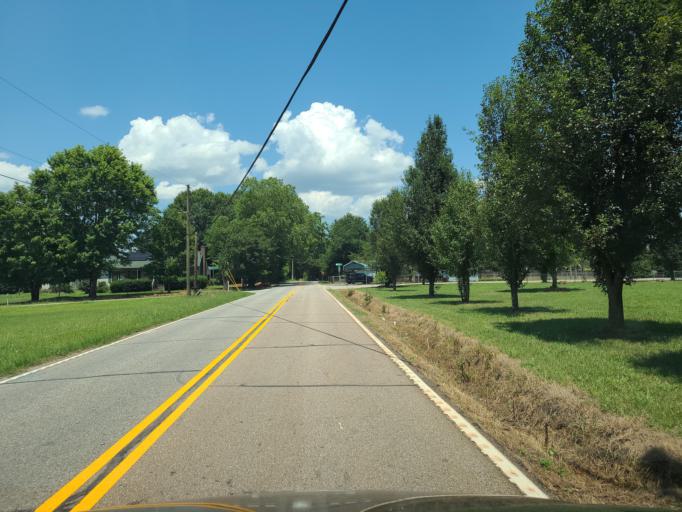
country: US
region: South Carolina
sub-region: Spartanburg County
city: Duncan
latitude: 34.9936
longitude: -82.1777
